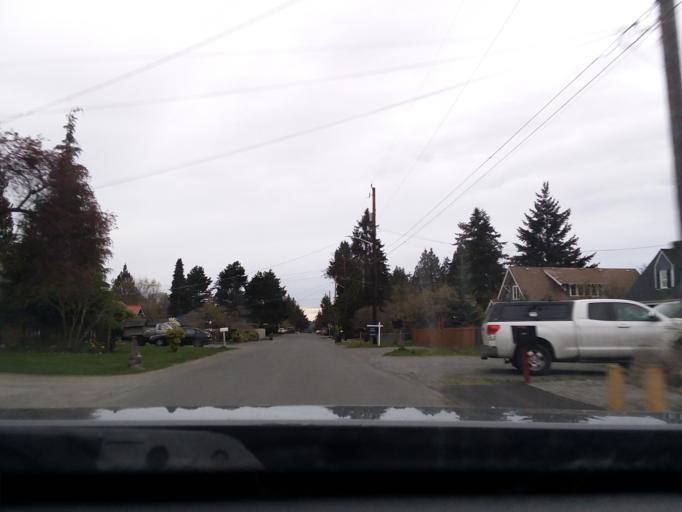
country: US
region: Washington
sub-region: King County
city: Shoreline
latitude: 47.7004
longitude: -122.3741
